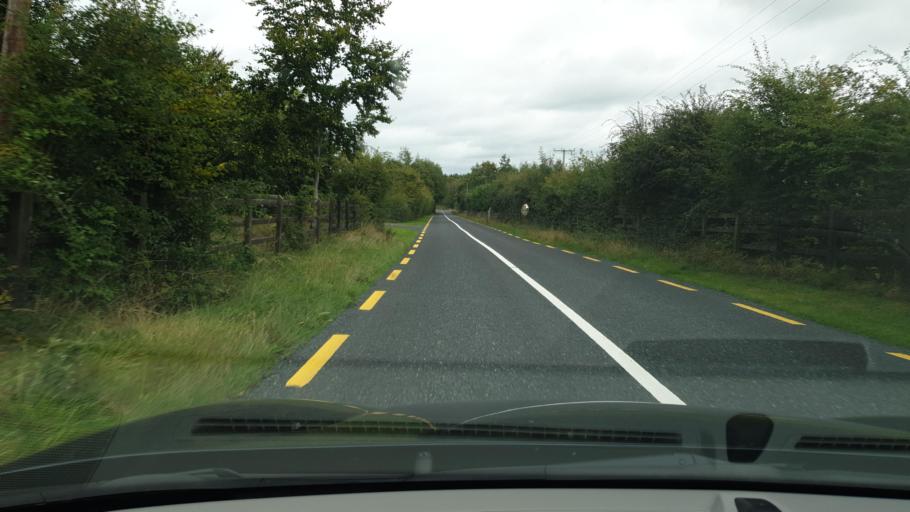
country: IE
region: Leinster
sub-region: Kildare
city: Naas
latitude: 53.2273
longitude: -6.7056
